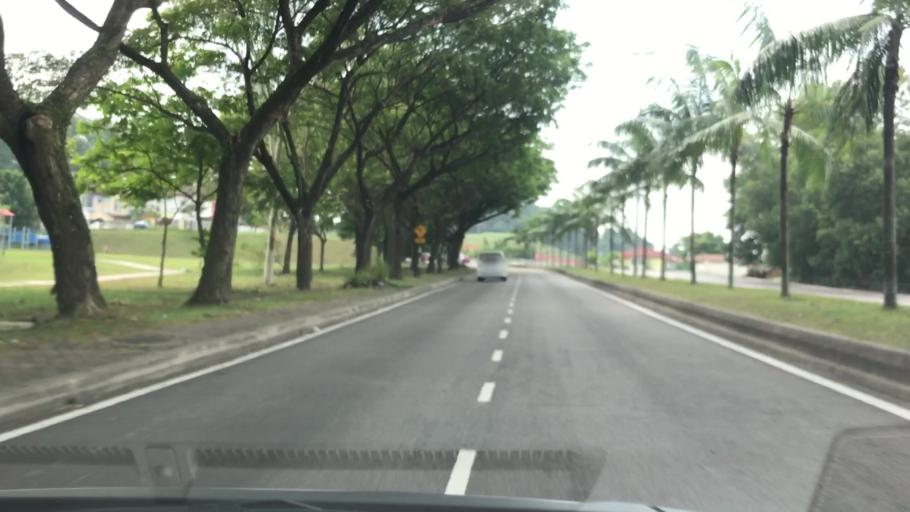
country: MY
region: Selangor
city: Kampong Baharu Balakong
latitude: 3.0242
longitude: 101.6781
